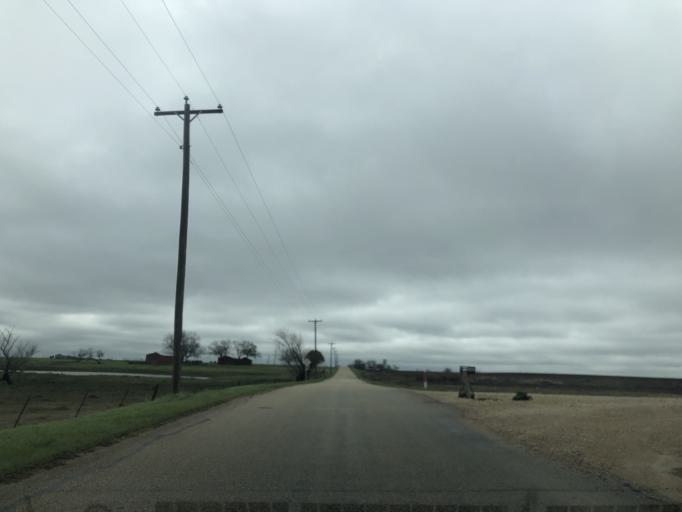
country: US
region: Texas
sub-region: Williamson County
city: Hutto
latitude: 30.5815
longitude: -97.4963
